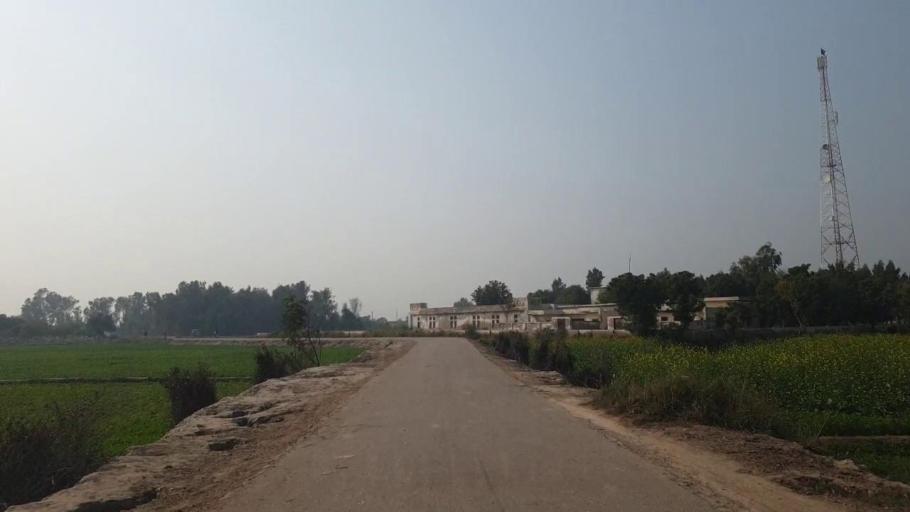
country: PK
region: Sindh
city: Shahdadpur
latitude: 26.0252
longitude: 68.5452
